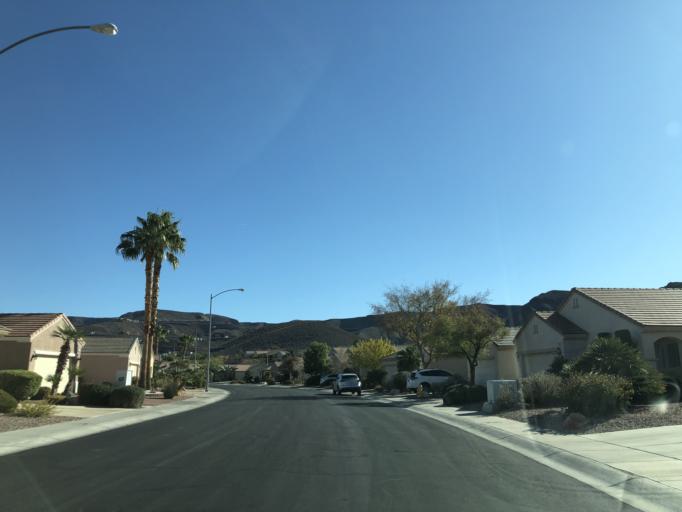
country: US
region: Nevada
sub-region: Clark County
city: Whitney
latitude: 36.0024
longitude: -115.0746
